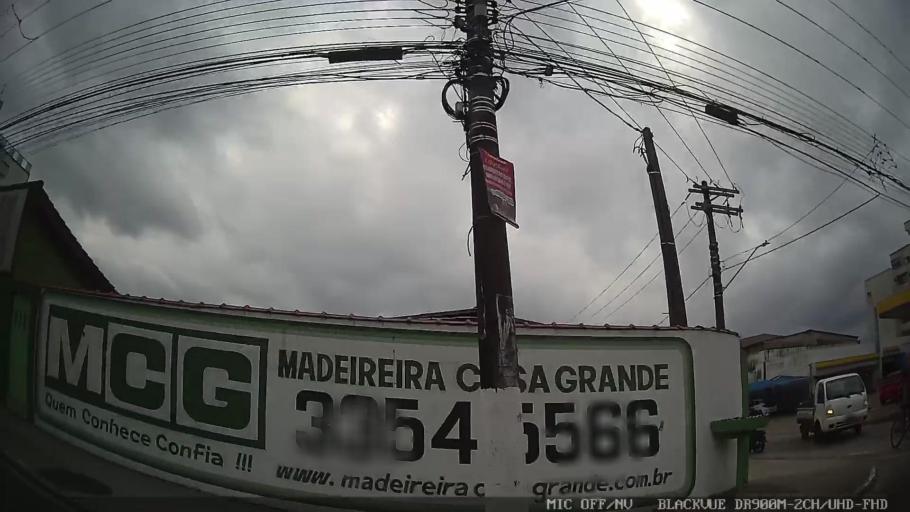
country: BR
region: Sao Paulo
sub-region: Guaruja
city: Guaruja
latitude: -24.0056
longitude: -46.2739
